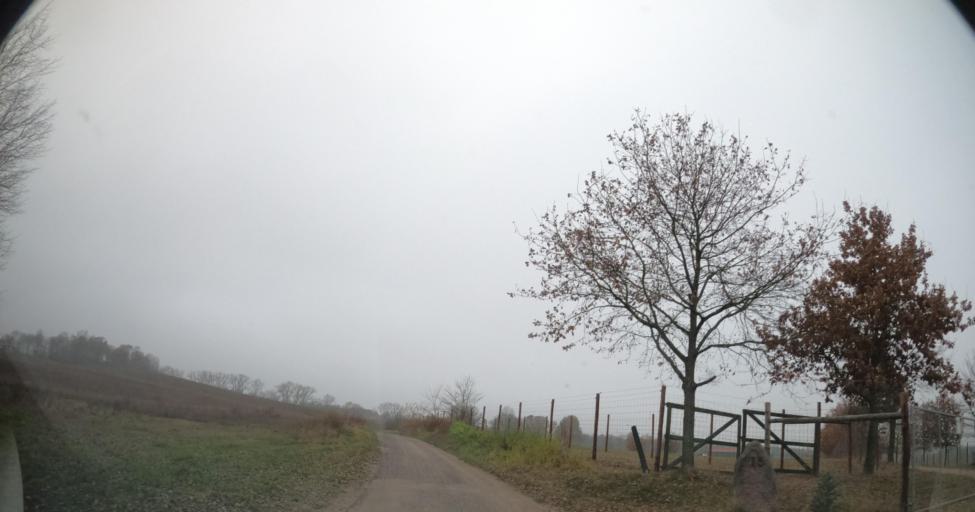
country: PL
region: West Pomeranian Voivodeship
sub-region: Powiat drawski
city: Drawsko Pomorskie
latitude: 53.5754
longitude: 15.8257
